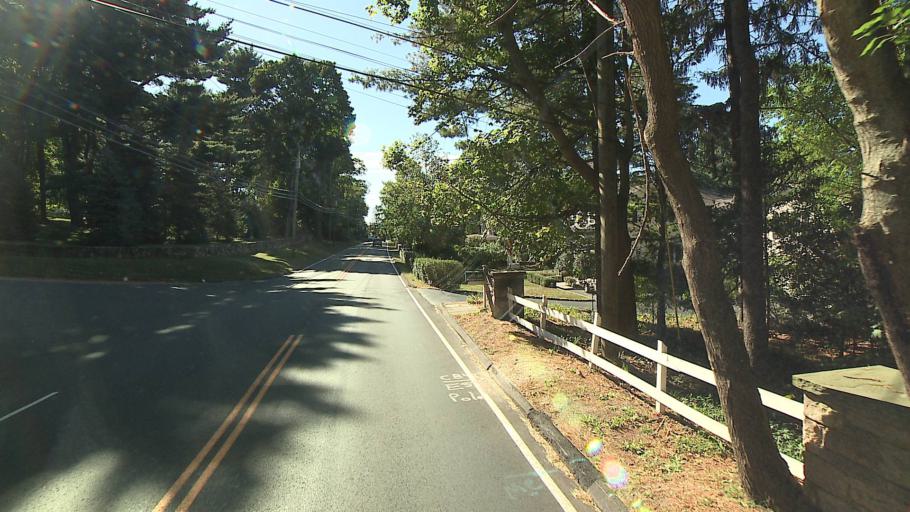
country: US
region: Connecticut
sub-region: Fairfield County
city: Darien
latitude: 41.1051
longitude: -73.4838
